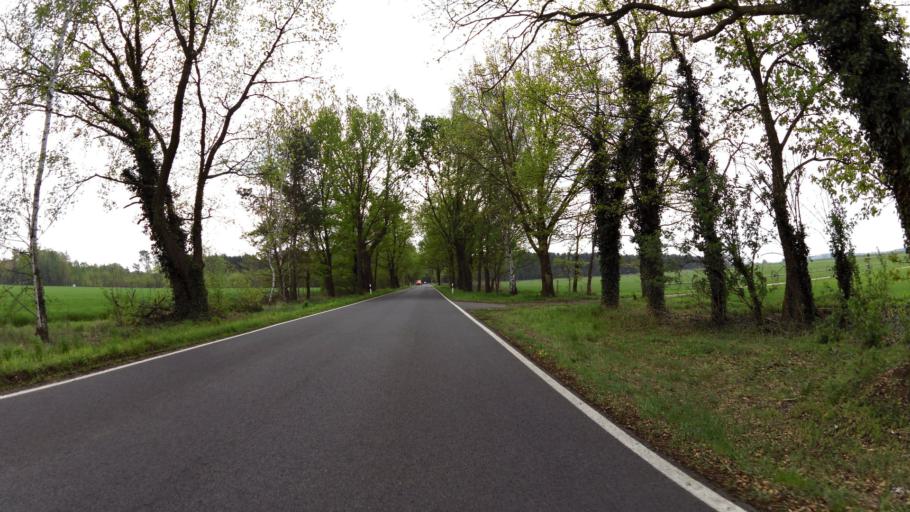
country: DE
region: Brandenburg
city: Bestensee
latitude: 52.2666
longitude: 13.7337
